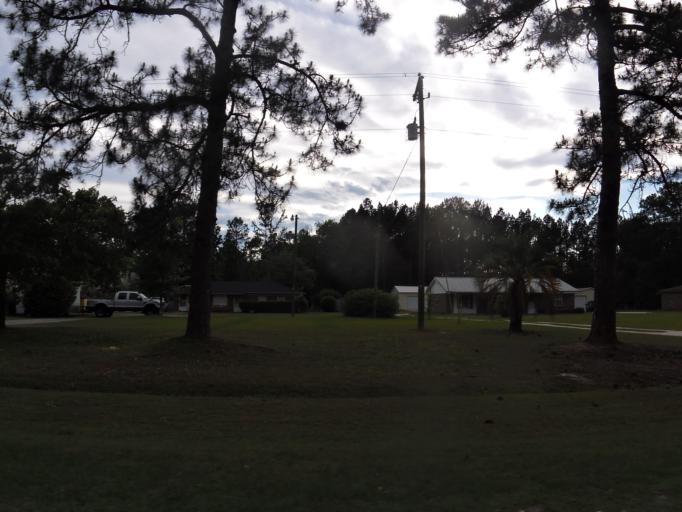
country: US
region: South Carolina
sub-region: Jasper County
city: Hardeeville
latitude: 32.3105
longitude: -81.0879
